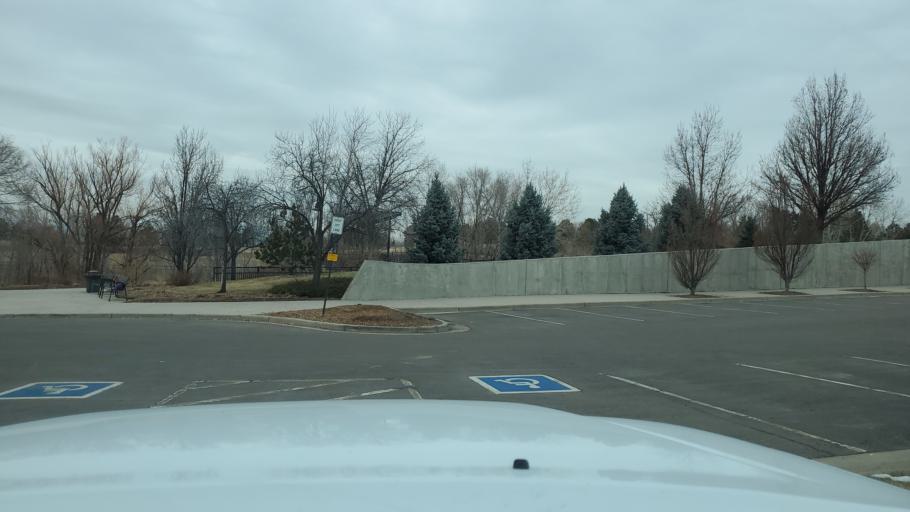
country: US
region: Colorado
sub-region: Arapahoe County
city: Castlewood
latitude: 39.6121
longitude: -104.9057
